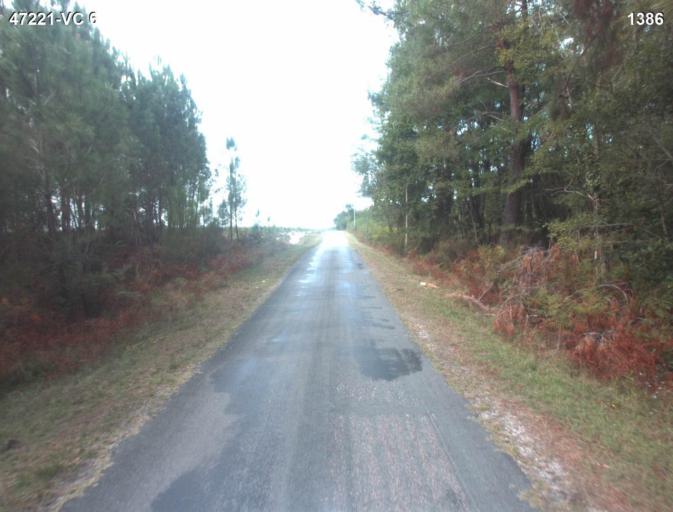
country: FR
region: Aquitaine
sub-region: Departement du Lot-et-Garonne
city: Mezin
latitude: 44.1027
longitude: 0.1647
